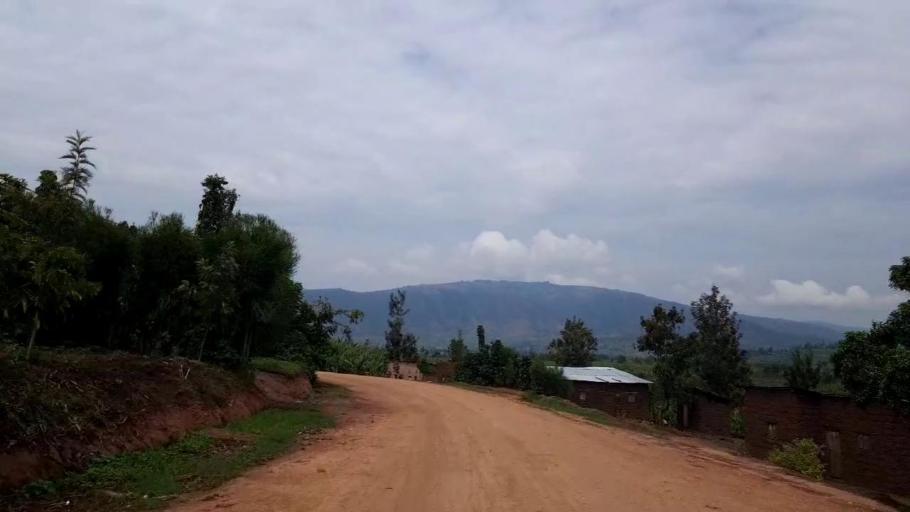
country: RW
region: Northern Province
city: Byumba
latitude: -1.4974
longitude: 30.2242
